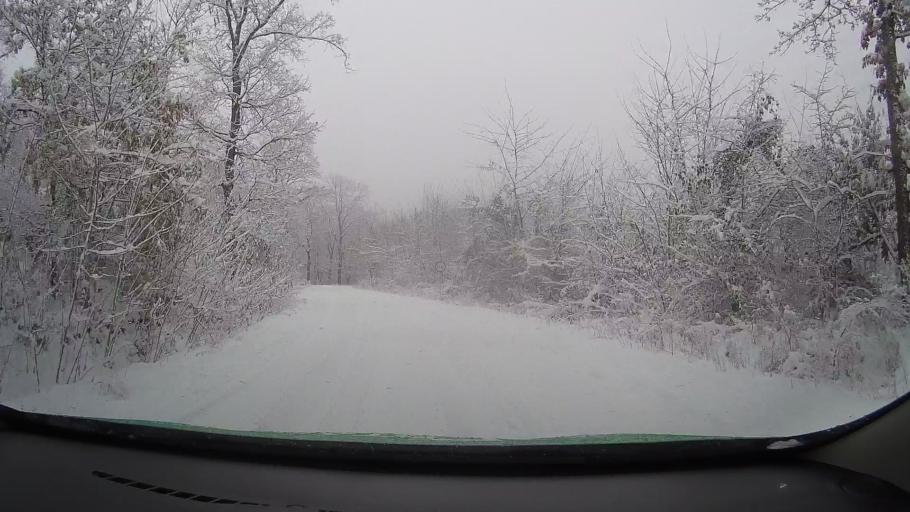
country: RO
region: Hunedoara
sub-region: Comuna Teliucu Inferior
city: Teliucu Inferior
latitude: 45.6887
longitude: 22.9014
